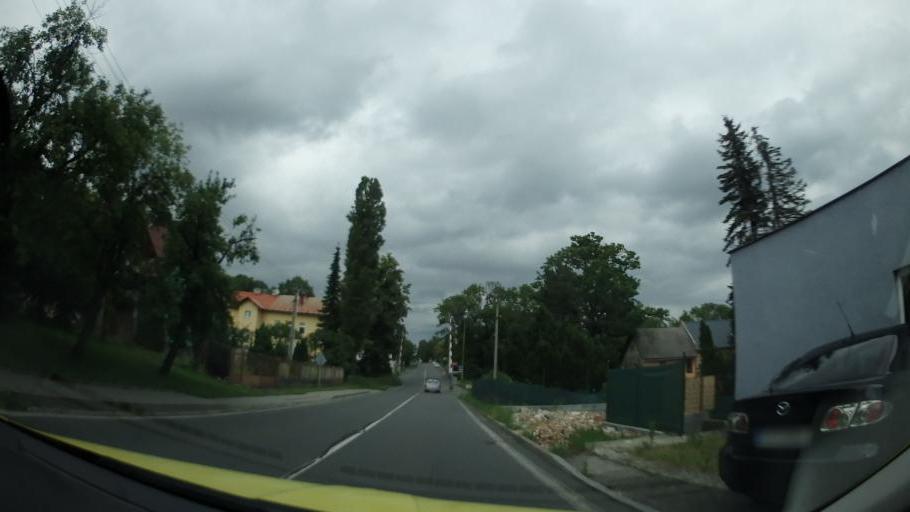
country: CZ
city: Stramberk
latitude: 49.5819
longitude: 18.1277
